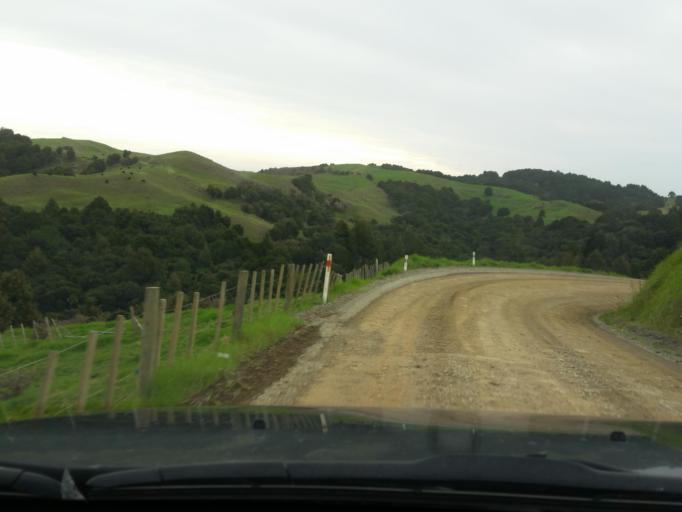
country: NZ
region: Auckland
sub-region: Auckland
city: Wellsford
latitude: -36.1435
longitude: 174.3528
